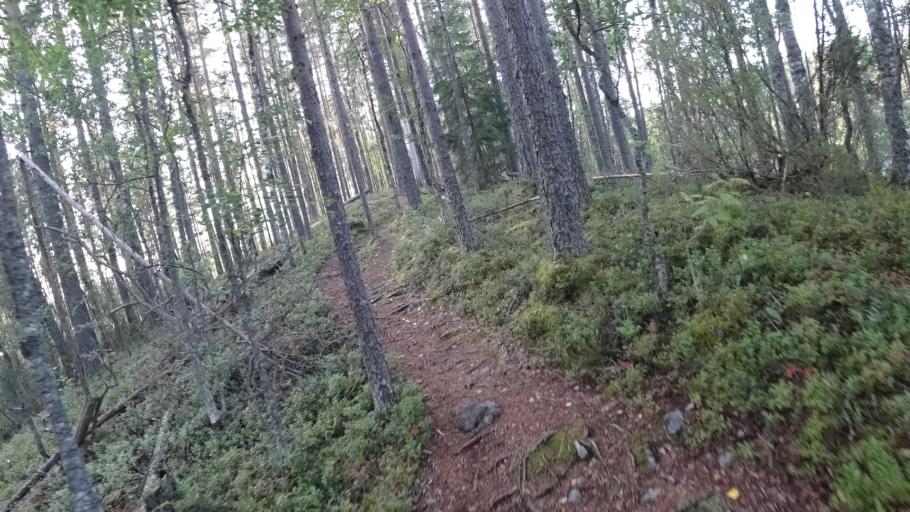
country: FI
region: North Karelia
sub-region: Joensuu
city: Ilomantsi
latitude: 62.5800
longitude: 31.1577
